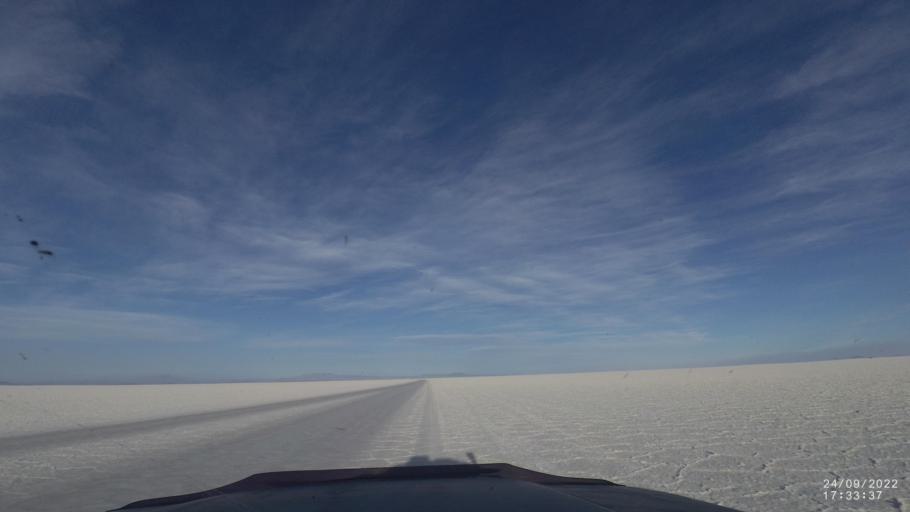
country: BO
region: Potosi
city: Colchani
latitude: -20.3200
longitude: -67.3014
